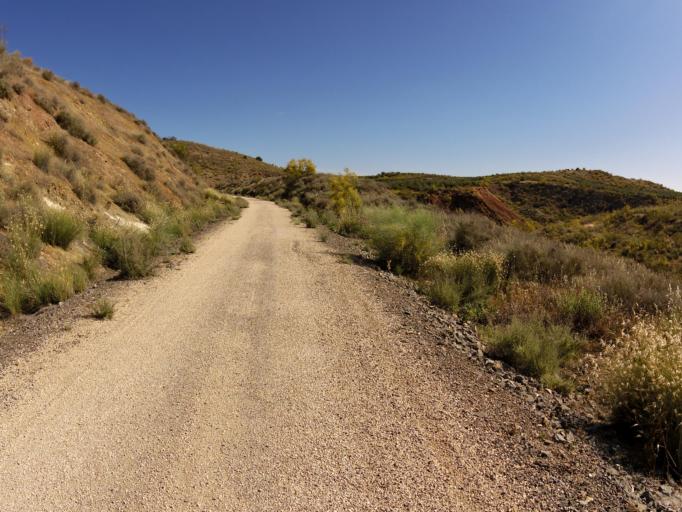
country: ES
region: Andalusia
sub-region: Provincia de Jaen
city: Alcaudete
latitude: 37.5964
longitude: -4.1559
